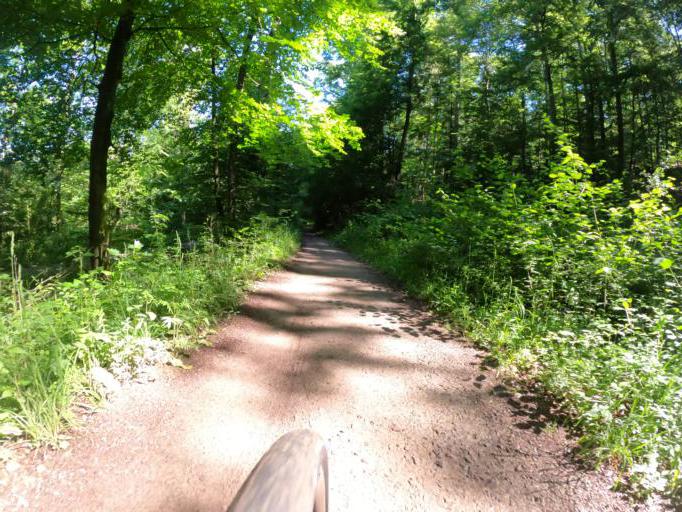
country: DE
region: Baden-Wuerttemberg
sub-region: Regierungsbezirk Stuttgart
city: Gerlingen
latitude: 48.7504
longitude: 9.0912
